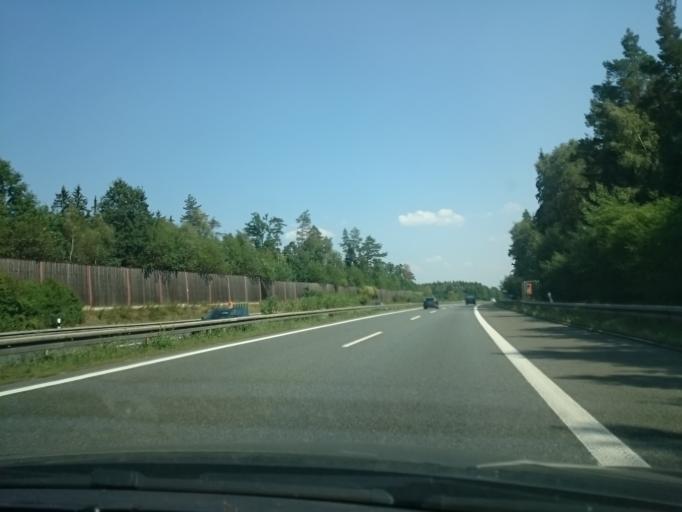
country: DE
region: Saxony
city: Hirschfeld
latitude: 50.6475
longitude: 12.4581
